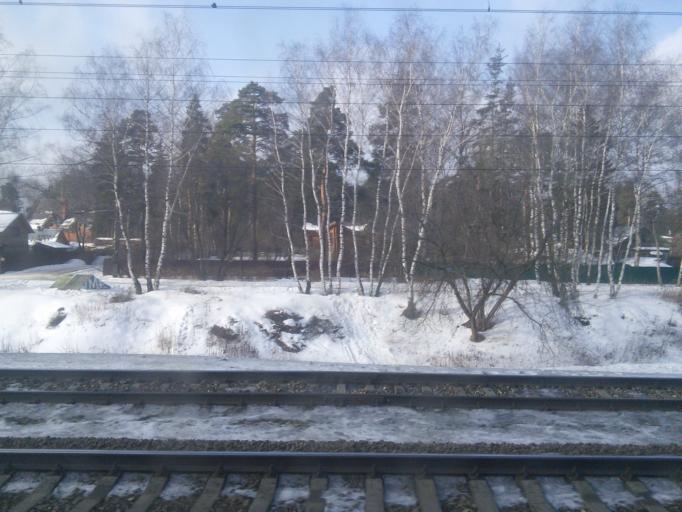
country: RU
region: Moskovskaya
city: Cherkizovo
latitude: 55.9567
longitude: 37.8054
